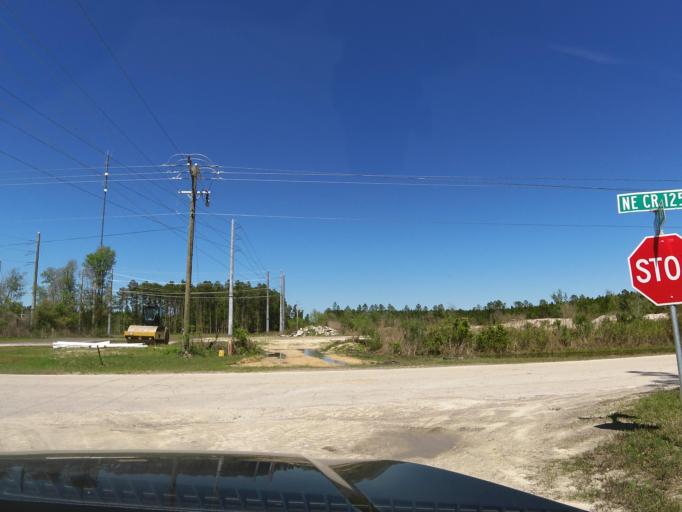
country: US
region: Florida
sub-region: Bradford County
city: Starke
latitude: 30.0558
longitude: -82.0555
